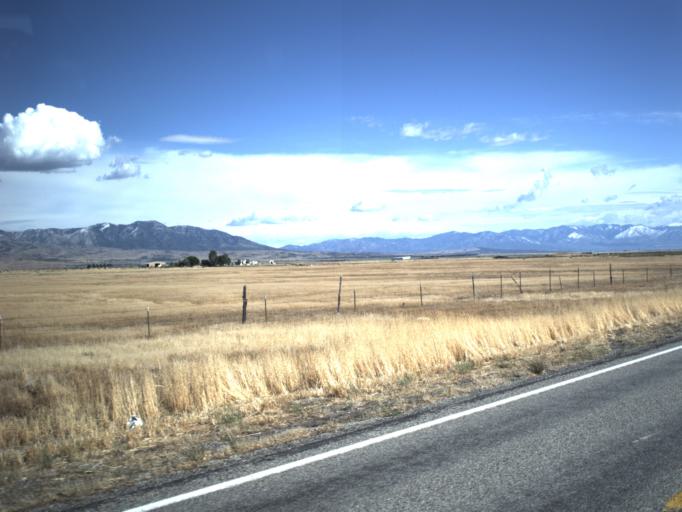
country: US
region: Utah
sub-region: Millard County
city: Delta
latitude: 39.3344
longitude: -112.4890
